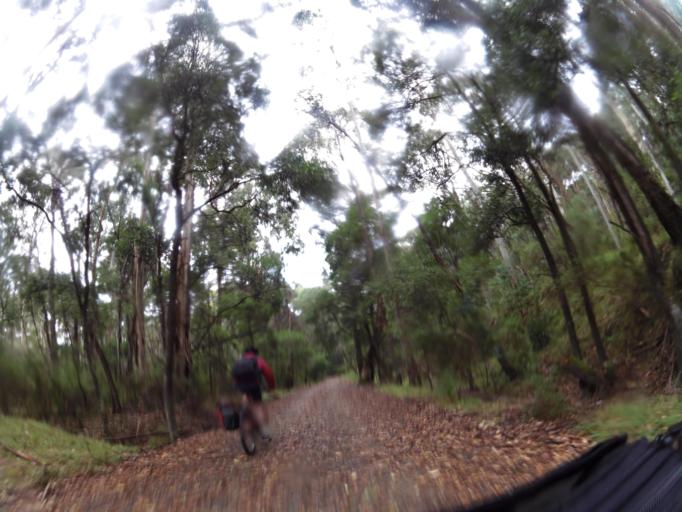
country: AU
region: New South Wales
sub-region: Greater Hume Shire
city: Holbrook
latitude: -36.1914
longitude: 147.5084
